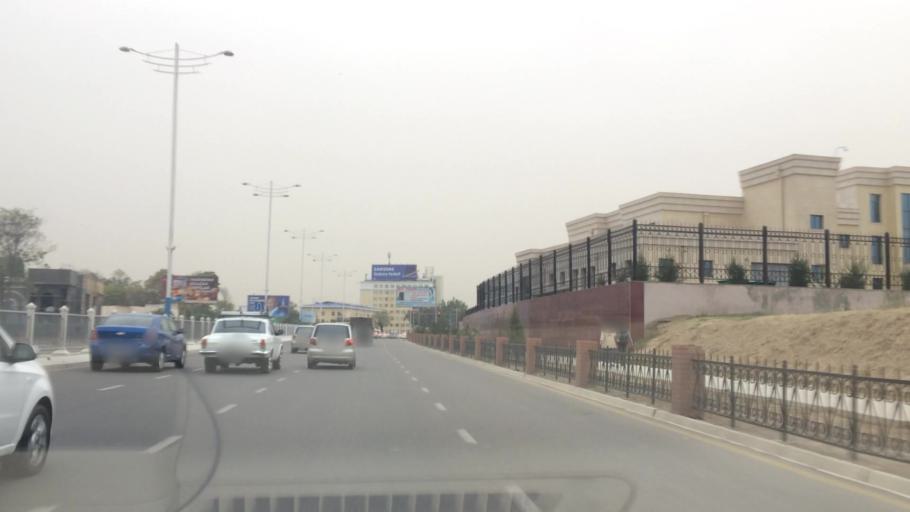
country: UZ
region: Toshkent Shahri
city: Bektemir
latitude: 41.3048
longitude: 69.3096
